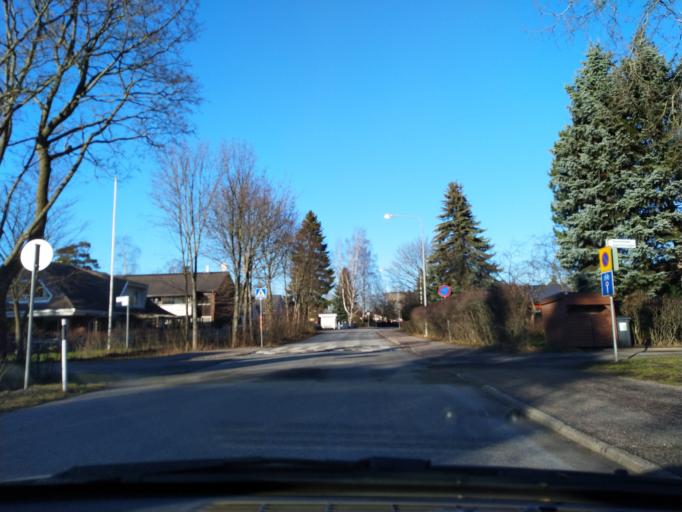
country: FI
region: Uusimaa
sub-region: Helsinki
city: Vantaa
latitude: 60.3023
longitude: 25.0389
